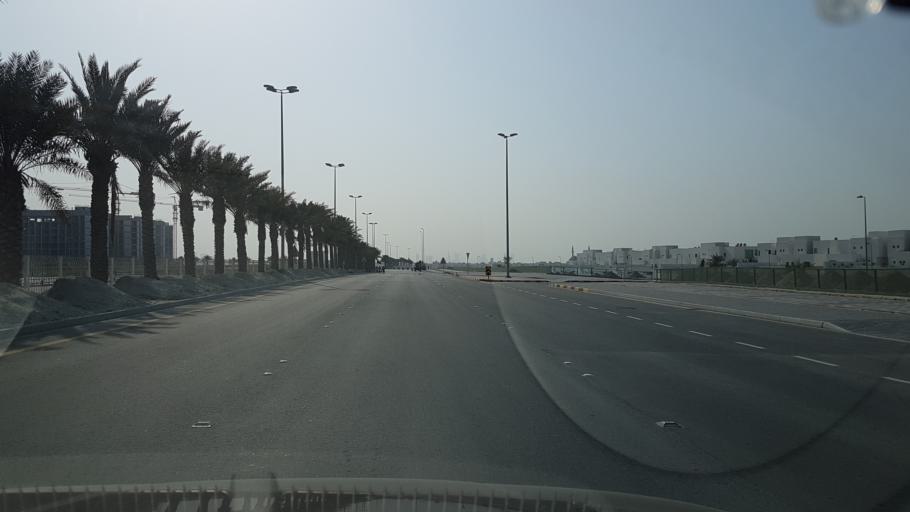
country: BH
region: Muharraq
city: Al Hadd
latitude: 26.2732
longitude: 50.6719
